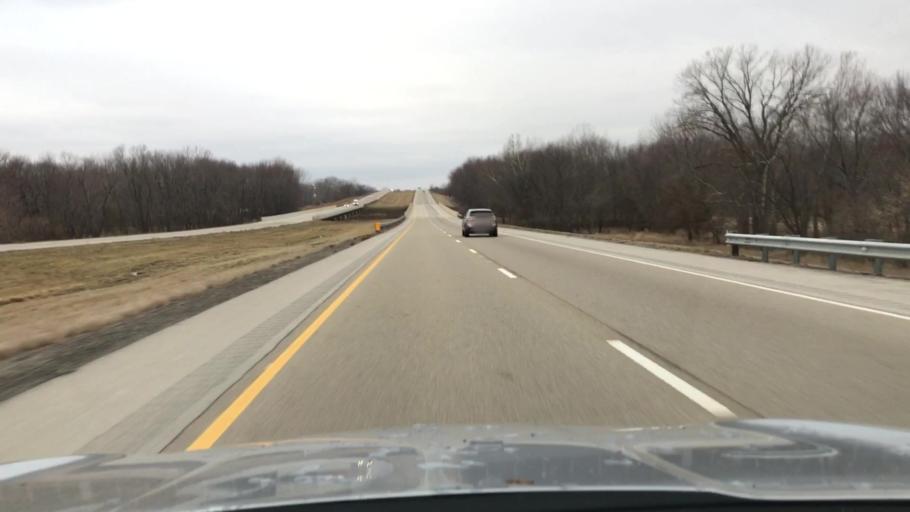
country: US
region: Illinois
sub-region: Logan County
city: Lincoln
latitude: 40.1812
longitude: -89.3665
